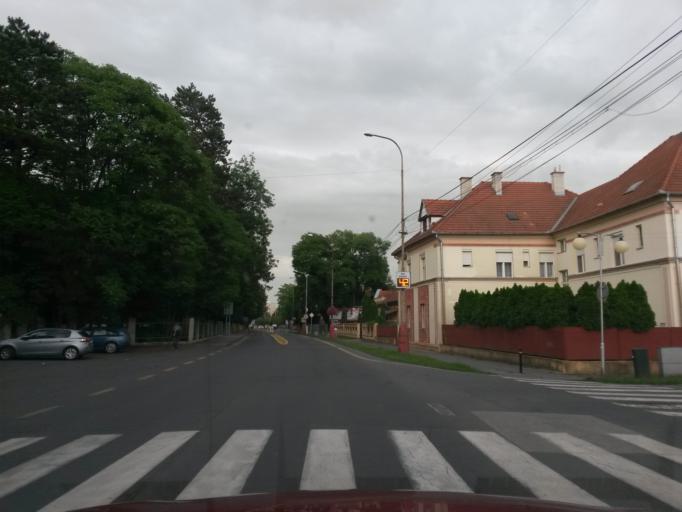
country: SK
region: Banskobystricky
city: Lucenec
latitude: 48.3300
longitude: 19.6545
